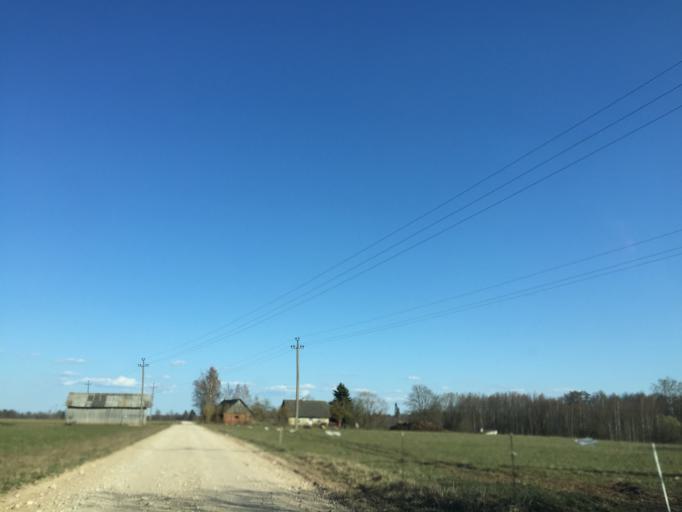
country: EE
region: Valgamaa
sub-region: Torva linn
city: Torva
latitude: 58.2399
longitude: 25.8960
